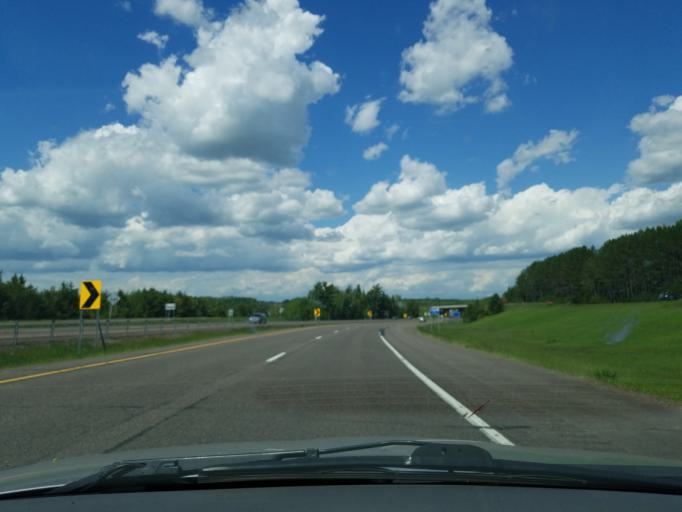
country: US
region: Minnesota
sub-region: Carlton County
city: Cloquet
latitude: 46.6869
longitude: -92.4590
